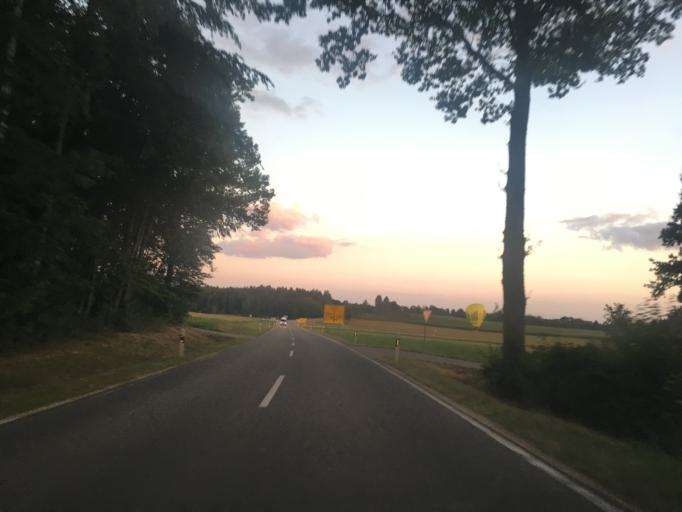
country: DE
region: Baden-Wuerttemberg
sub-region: Tuebingen Region
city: Hayingen
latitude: 48.2997
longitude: 9.4525
